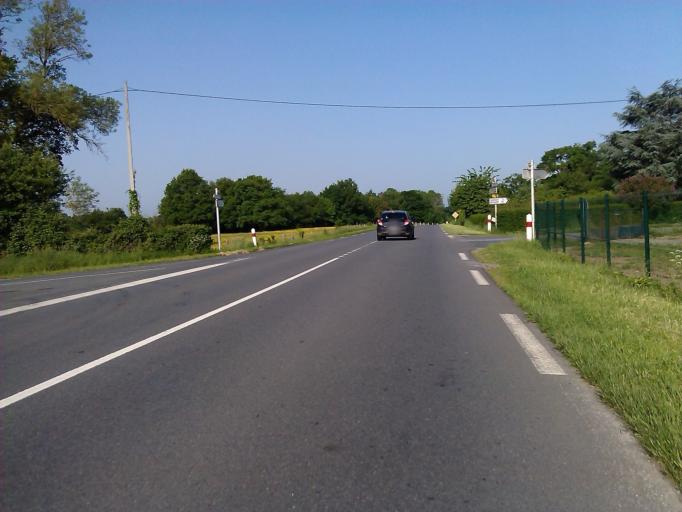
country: FR
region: Centre
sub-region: Departement de l'Indre
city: La Chatre
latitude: 46.5718
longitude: 1.9164
